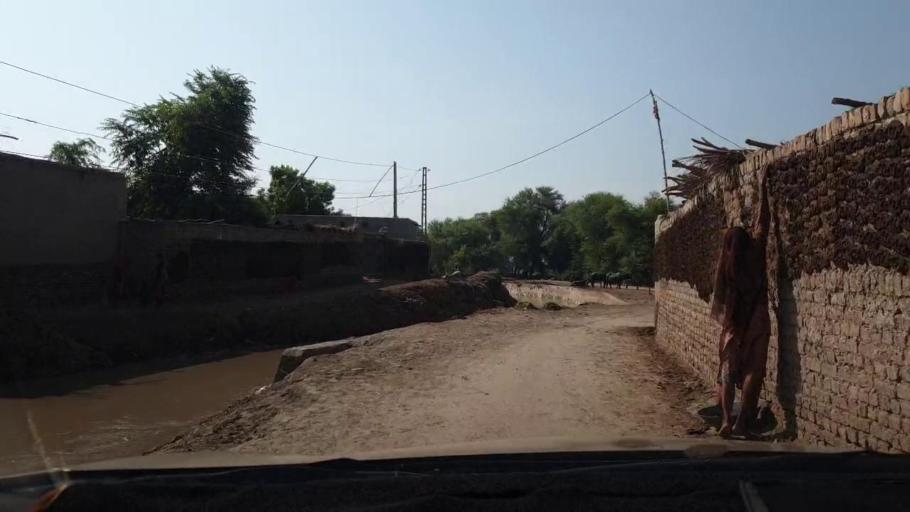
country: PK
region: Sindh
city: Larkana
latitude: 27.6237
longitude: 68.2611
